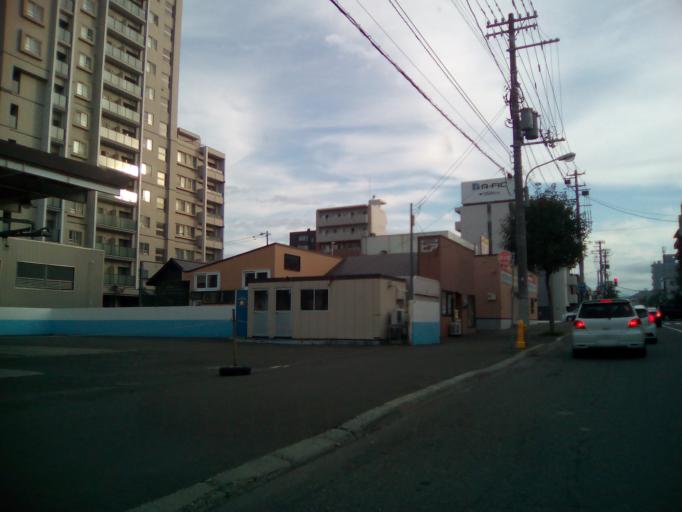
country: JP
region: Hokkaido
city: Sapporo
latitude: 43.0474
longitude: 141.3790
